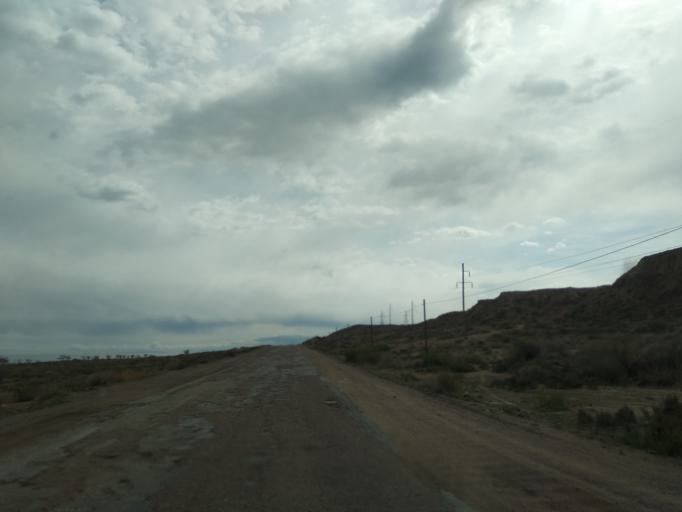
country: KG
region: Ysyk-Koel
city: Kadzhi-Say
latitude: 42.1794
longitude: 77.3175
